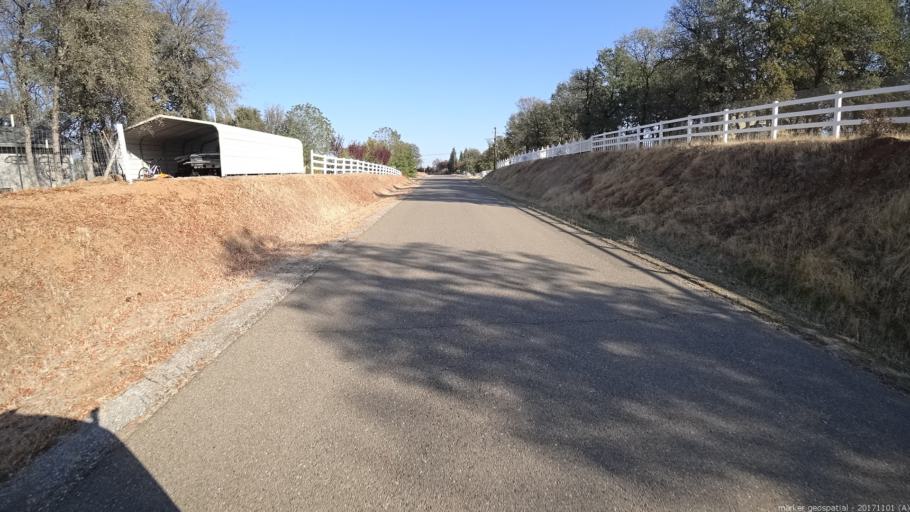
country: US
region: California
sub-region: Shasta County
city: Bella Vista
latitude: 40.6714
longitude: -122.2974
